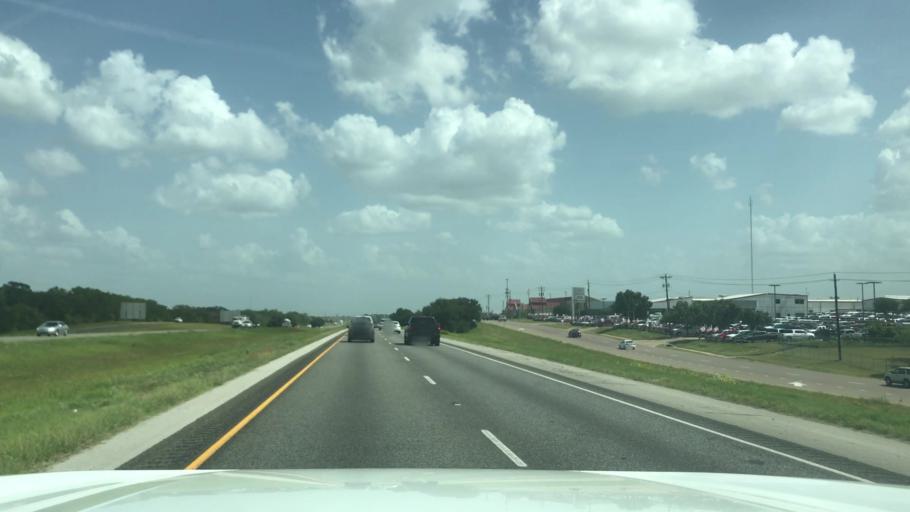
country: US
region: Texas
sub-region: Brazos County
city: College Station
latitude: 30.6558
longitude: -96.3220
